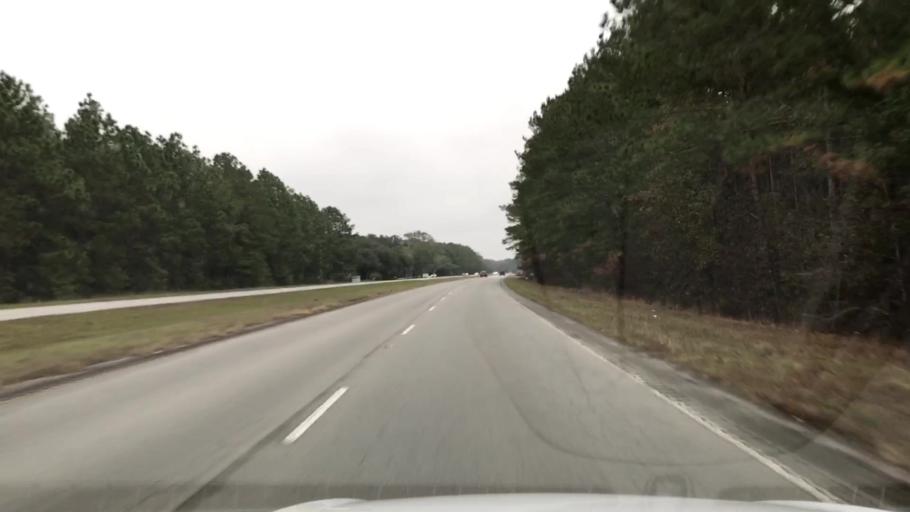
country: US
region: South Carolina
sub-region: Charleston County
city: Awendaw
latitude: 32.9803
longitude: -79.6613
